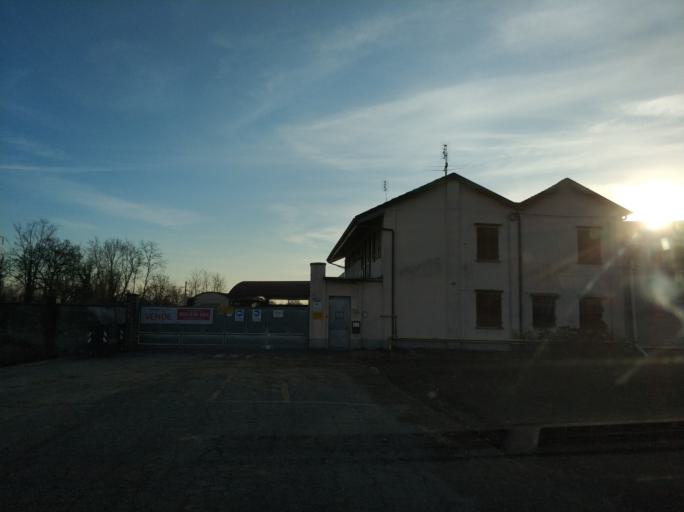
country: IT
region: Piedmont
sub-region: Provincia di Torino
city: San Francesco al Campo
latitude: 45.2231
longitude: 7.6438
